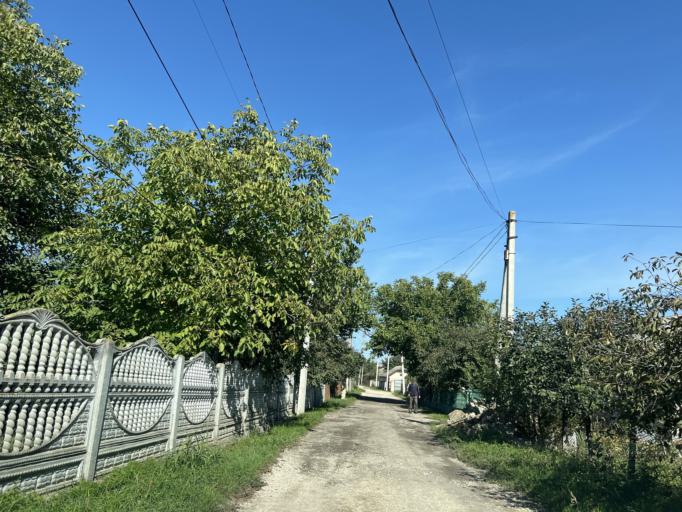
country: RO
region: Iasi
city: Ungheni-Prut
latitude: 47.1942
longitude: 27.7917
